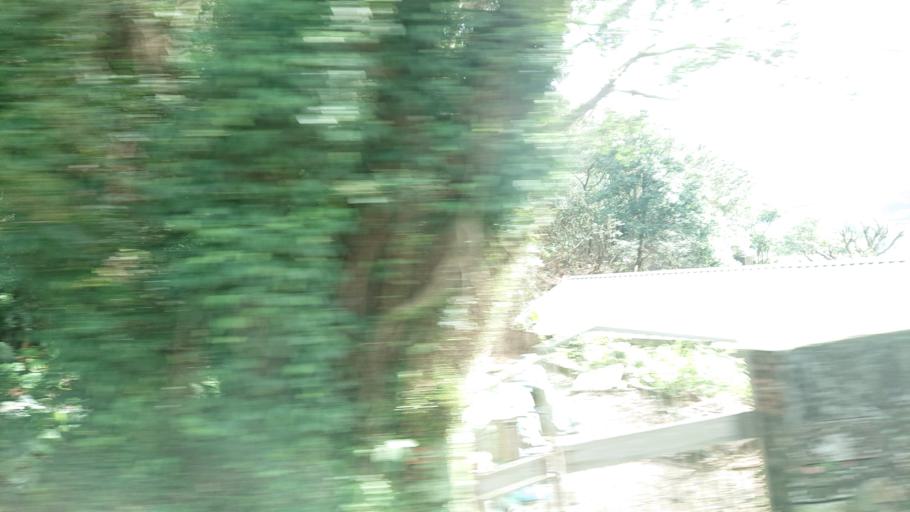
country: TW
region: Taiwan
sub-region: Keelung
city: Keelung
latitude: 25.1107
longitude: 121.8497
